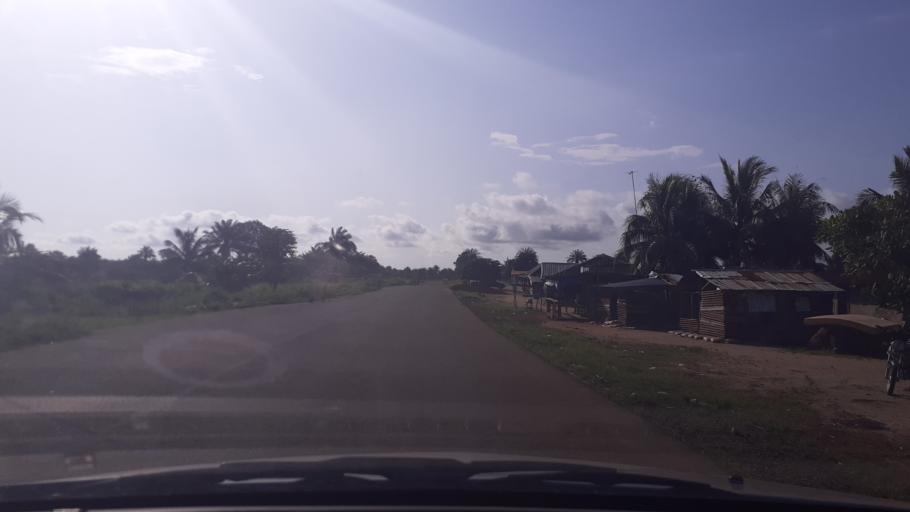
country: LR
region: Montserrado
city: Bensonville City
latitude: 6.1686
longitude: -10.4456
